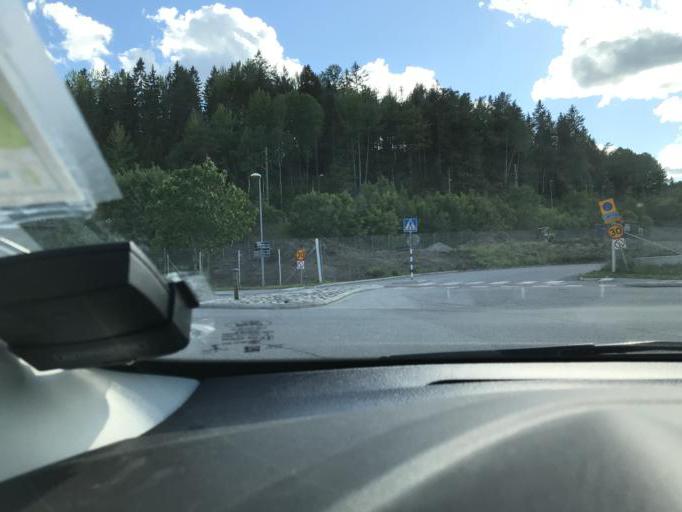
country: SE
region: Stockholm
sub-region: Botkyrka Kommun
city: Tumba
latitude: 59.2006
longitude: 17.8268
